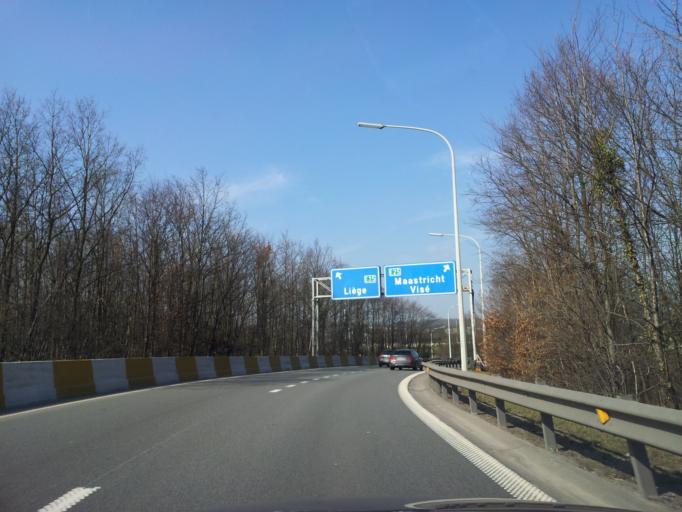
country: BE
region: Wallonia
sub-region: Province de Liege
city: Oupeye
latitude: 50.6801
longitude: 5.6616
